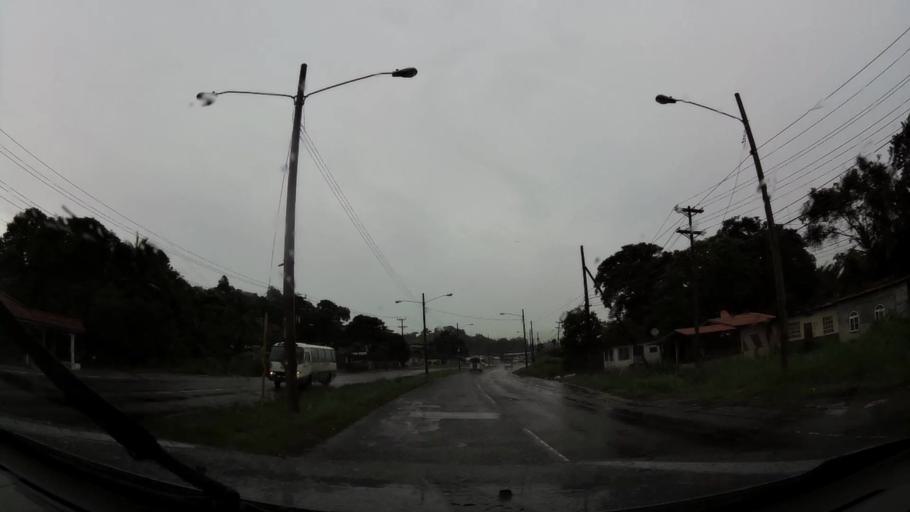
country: PA
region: Colon
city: Cativa
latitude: 9.3601
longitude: -79.8279
